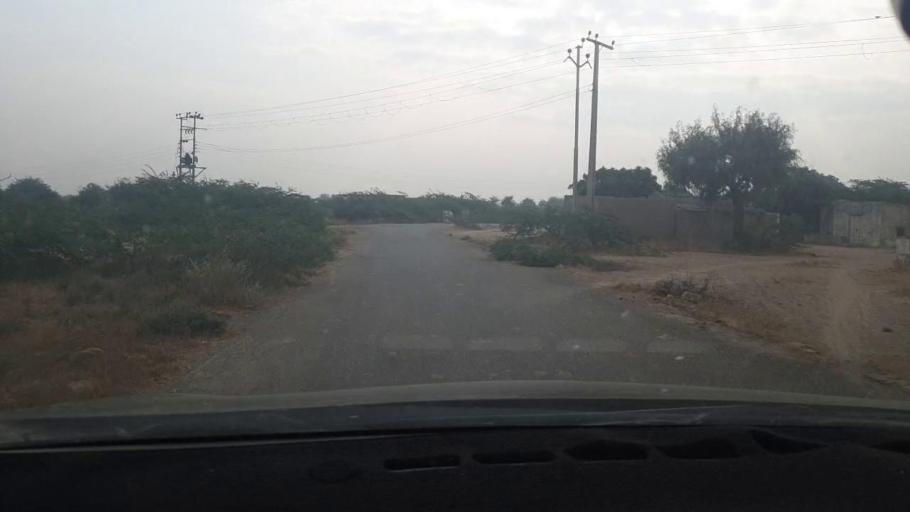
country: PK
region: Sindh
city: Malir Cantonment
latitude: 24.9558
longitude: 67.4093
